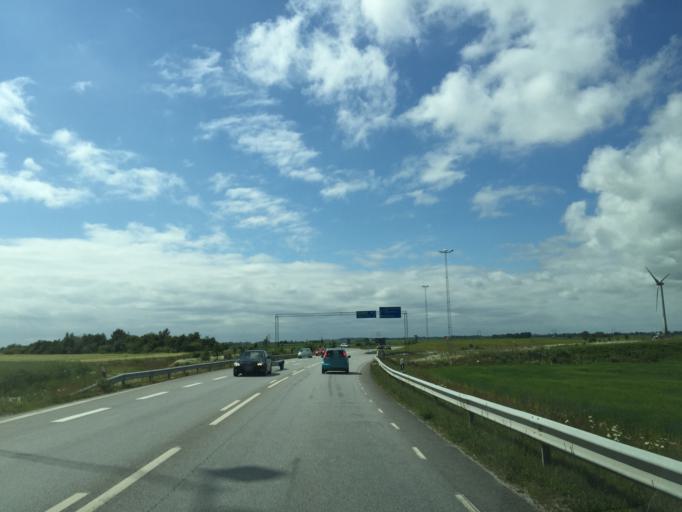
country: SE
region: Skane
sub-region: Staffanstorps Kommun
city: Hjaerup
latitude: 55.6945
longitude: 13.1362
